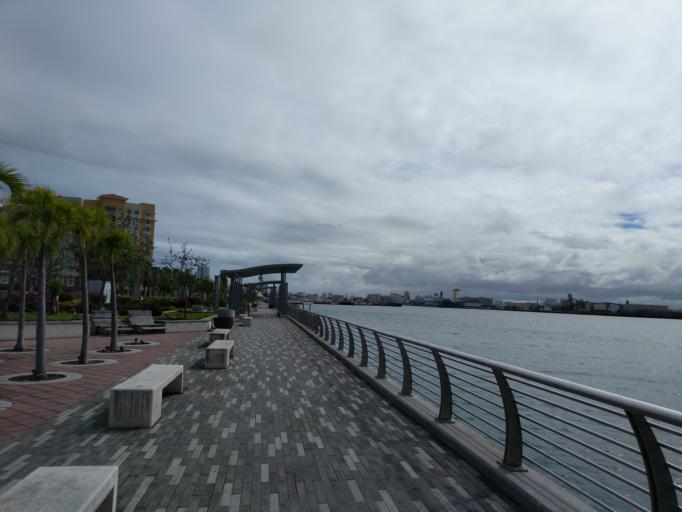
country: PR
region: San Juan
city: San Juan
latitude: 18.4636
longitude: -66.1098
